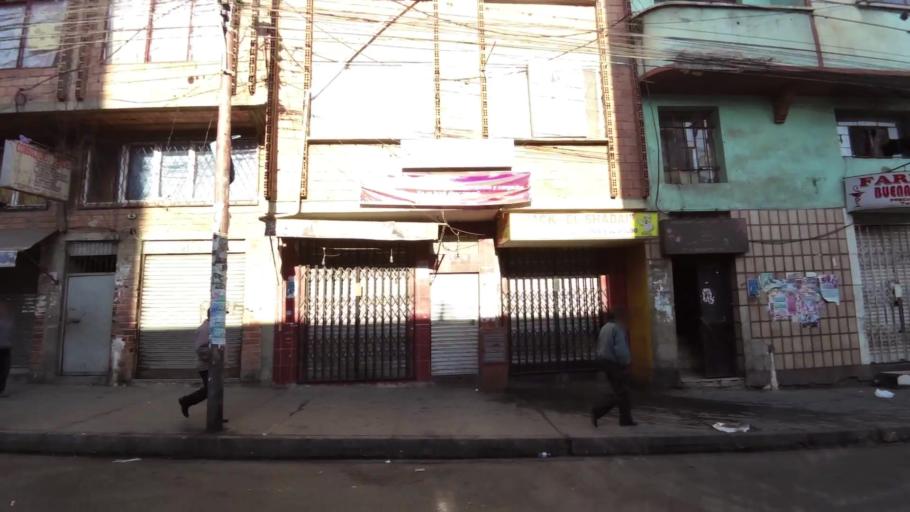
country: BO
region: La Paz
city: La Paz
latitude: -16.5027
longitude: -68.1444
